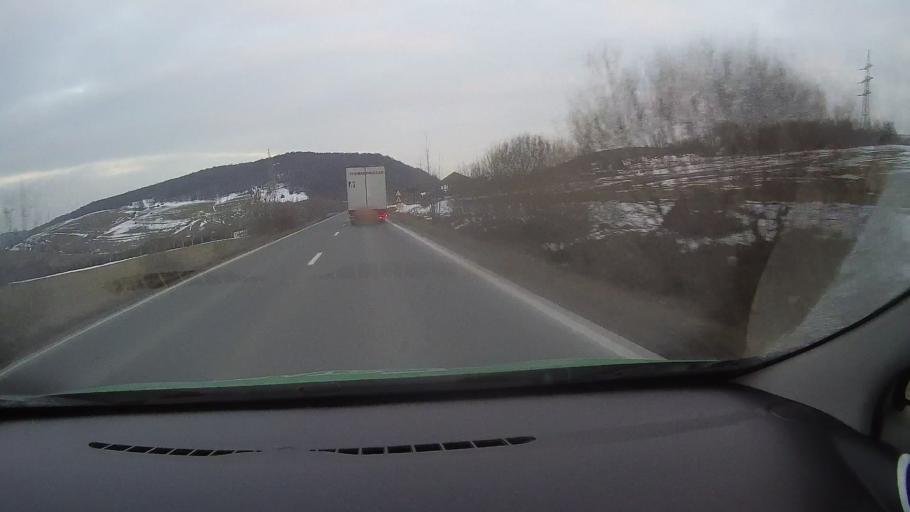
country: RO
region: Harghita
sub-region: Municipiul Odorheiu Secuiesc
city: Odorheiu Secuiesc
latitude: 46.3433
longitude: 25.2678
